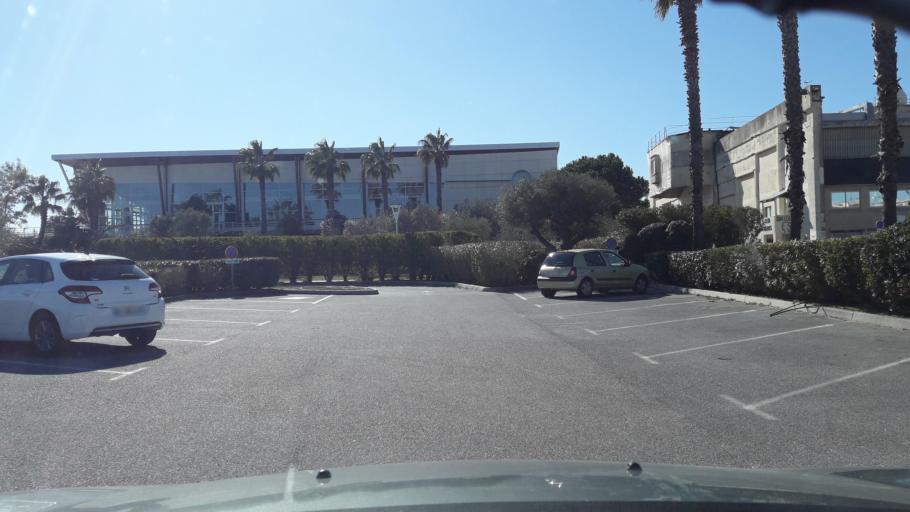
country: FR
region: Provence-Alpes-Cote d'Azur
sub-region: Departement du Var
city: Frejus
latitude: 43.4175
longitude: 6.7436
